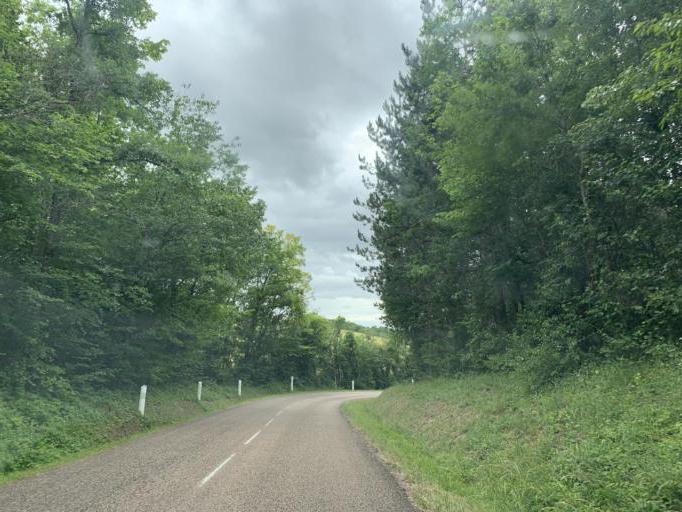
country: FR
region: Bourgogne
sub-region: Departement de l'Yonne
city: Saint-Bris-le-Vineux
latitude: 47.7222
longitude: 3.6929
